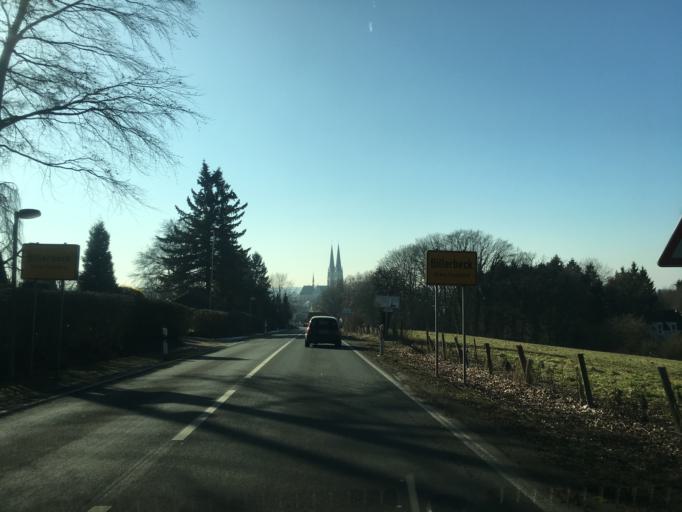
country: DE
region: North Rhine-Westphalia
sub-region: Regierungsbezirk Munster
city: Billerbeck
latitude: 51.9815
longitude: 7.3018
